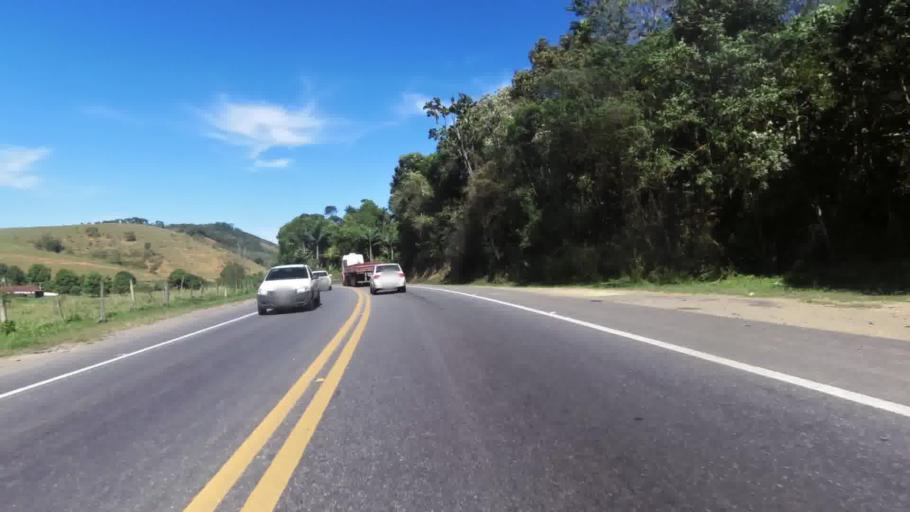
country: BR
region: Espirito Santo
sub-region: Iconha
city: Iconha
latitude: -20.8197
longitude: -40.8461
